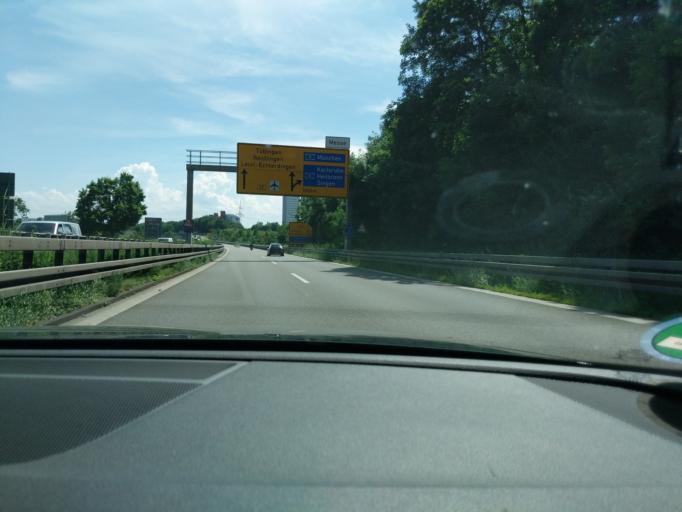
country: DE
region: Baden-Wuerttemberg
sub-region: Regierungsbezirk Stuttgart
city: Leinfelden-Echterdingen
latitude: 48.7194
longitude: 9.1631
